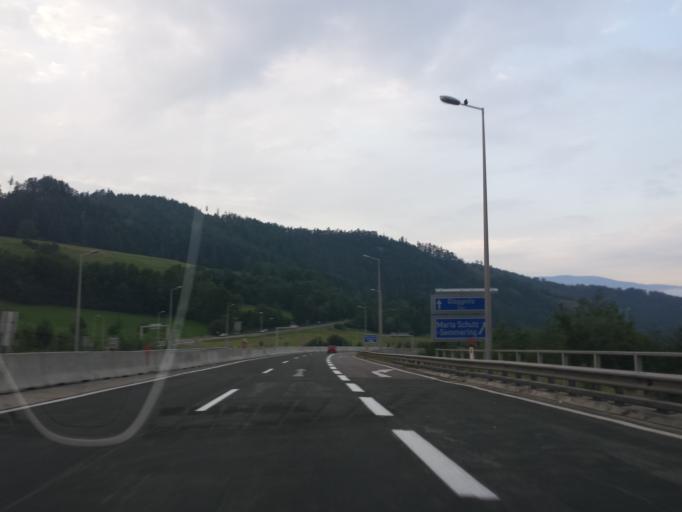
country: AT
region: Lower Austria
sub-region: Politischer Bezirk Neunkirchen
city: Semmering
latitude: 47.6396
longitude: 15.8499
